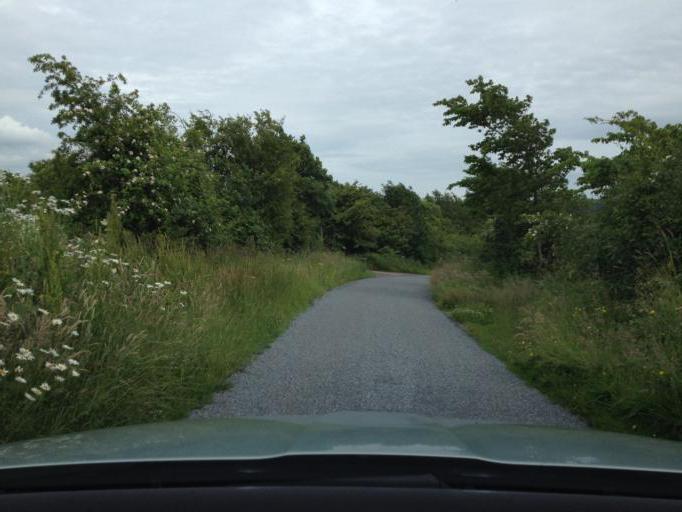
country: GB
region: Scotland
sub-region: Perth and Kinross
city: Bridge of Earn
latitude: 56.3273
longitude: -3.4006
